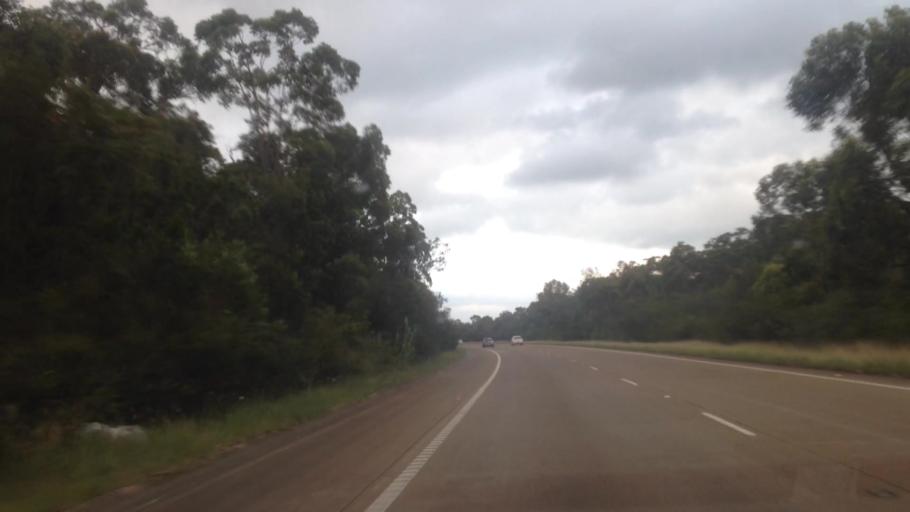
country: AU
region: New South Wales
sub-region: Lake Macquarie Shire
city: Dora Creek
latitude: -33.1465
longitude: 151.4749
